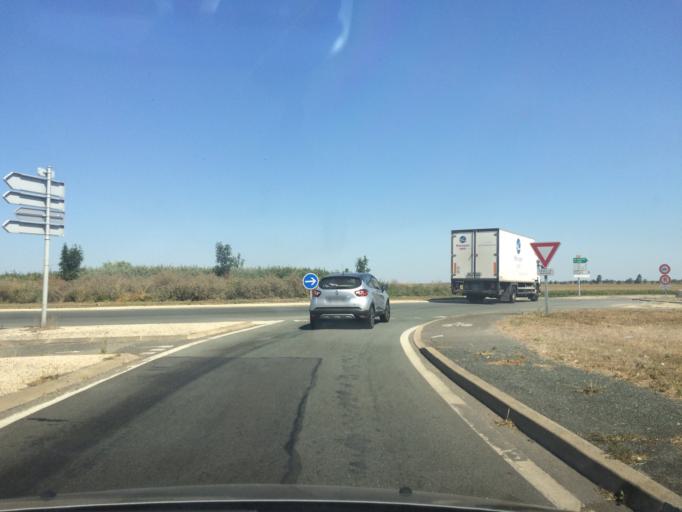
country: FR
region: Poitou-Charentes
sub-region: Departement de la Charente-Maritime
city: Esnandes
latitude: 46.2422
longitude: -1.0789
